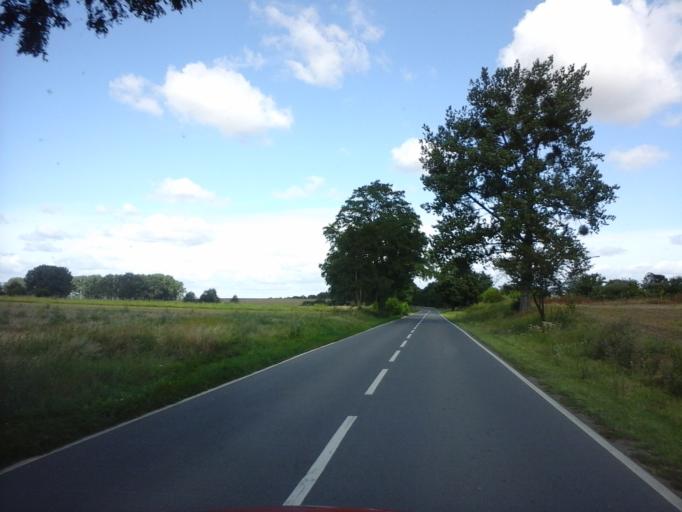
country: PL
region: West Pomeranian Voivodeship
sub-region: Powiat stargardzki
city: Dolice
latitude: 53.1934
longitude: 15.1923
